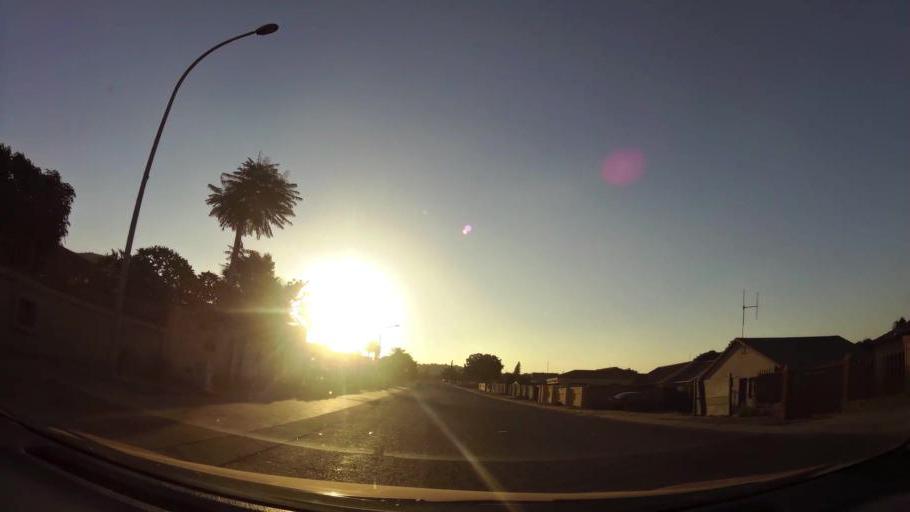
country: ZA
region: North-West
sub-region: Bojanala Platinum District Municipality
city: Rustenburg
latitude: -25.6404
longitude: 27.2051
